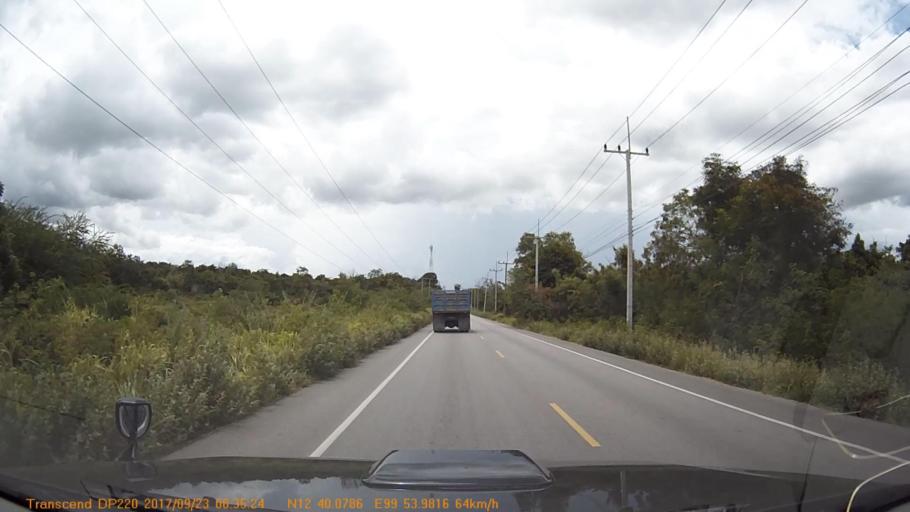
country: TH
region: Prachuap Khiri Khan
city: Hua Hin
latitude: 12.6680
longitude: 99.8994
